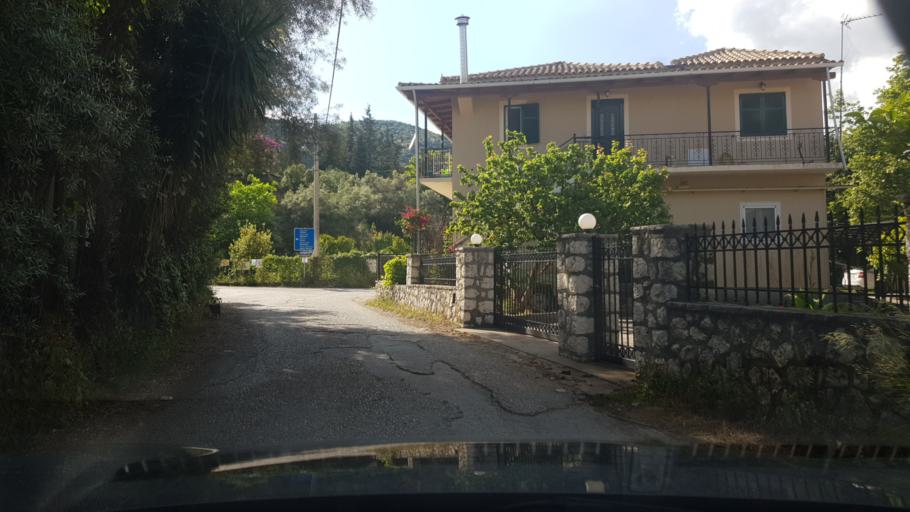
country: GR
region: Ionian Islands
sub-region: Lefkada
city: Nidri
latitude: 38.7151
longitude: 20.7006
